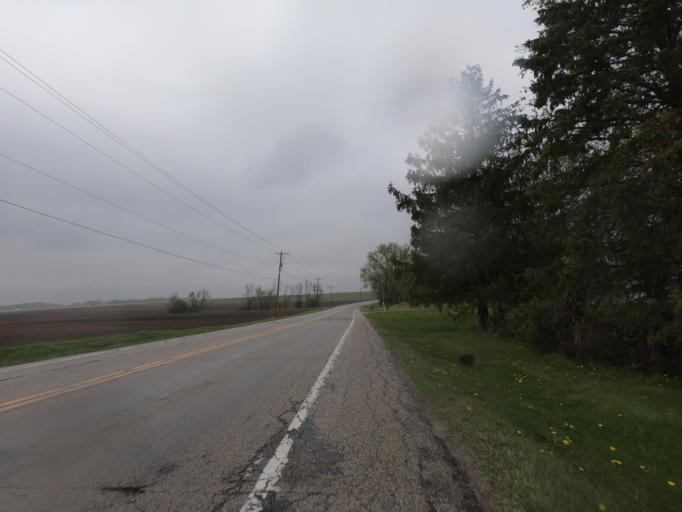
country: US
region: Wisconsin
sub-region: Jefferson County
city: Jefferson
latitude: 43.0251
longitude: -88.8185
